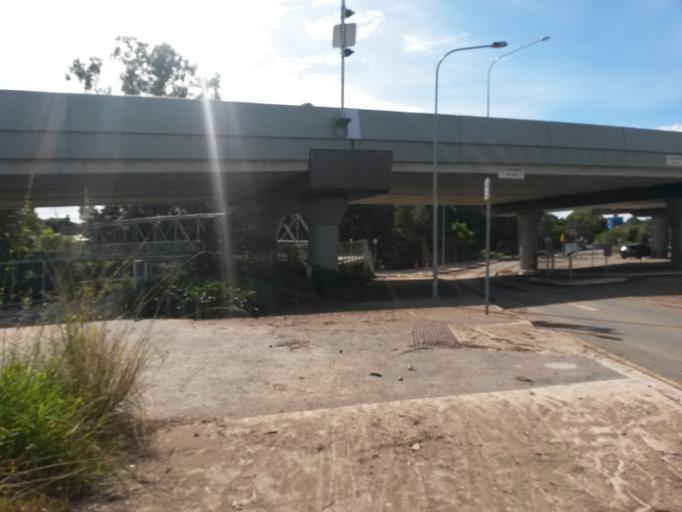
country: AU
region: Queensland
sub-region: Brisbane
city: Woolloongabba
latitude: -27.4978
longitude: 153.0434
